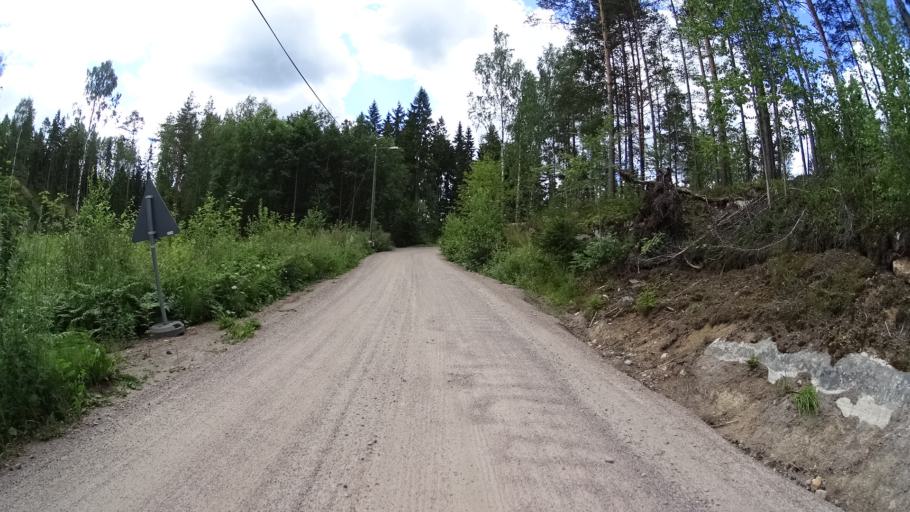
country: FI
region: Uusimaa
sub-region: Helsinki
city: Espoo
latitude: 60.2798
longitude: 24.5912
